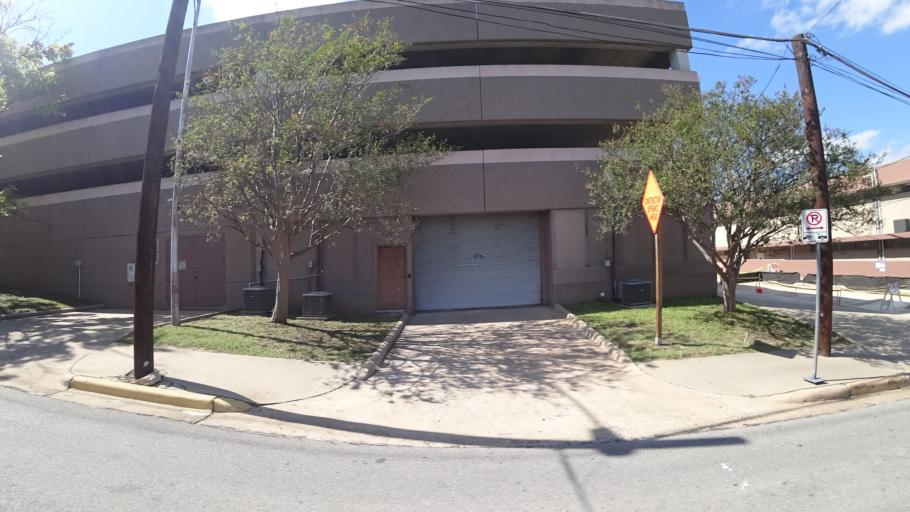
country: US
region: Texas
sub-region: Travis County
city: Austin
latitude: 30.2745
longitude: -97.7366
